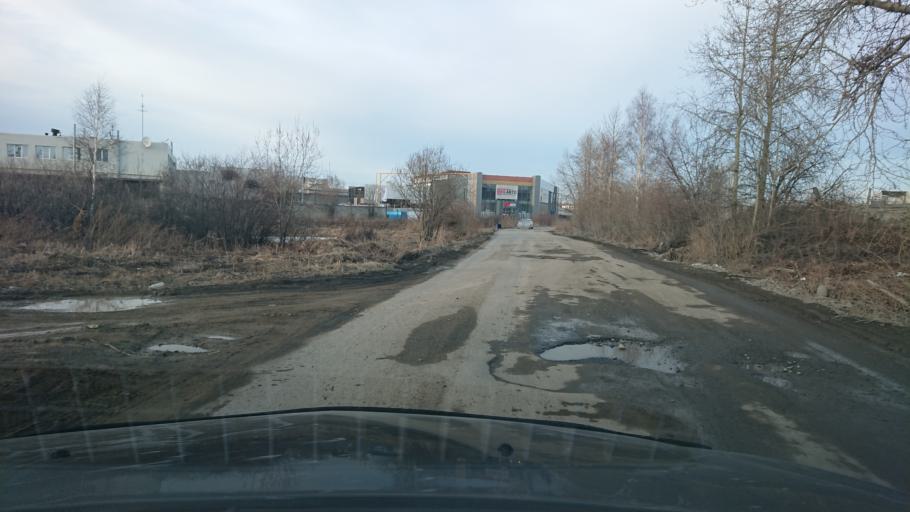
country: RU
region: Sverdlovsk
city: Sovkhoznyy
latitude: 56.7512
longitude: 60.6028
